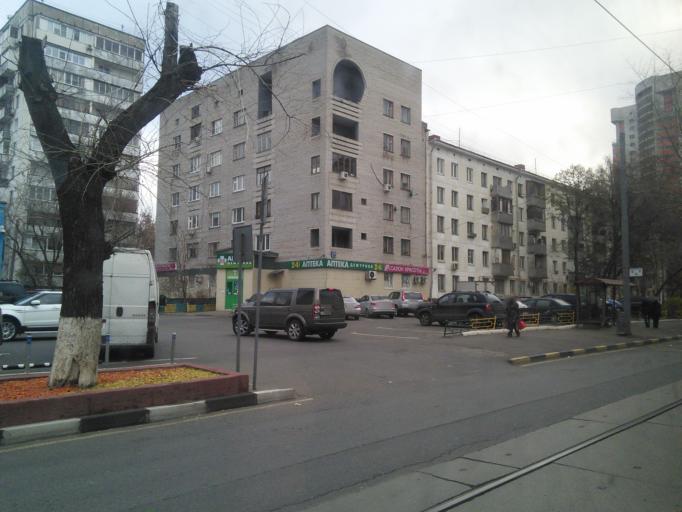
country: RU
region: Moscow
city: Lefortovo
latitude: 55.7614
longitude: 37.7123
